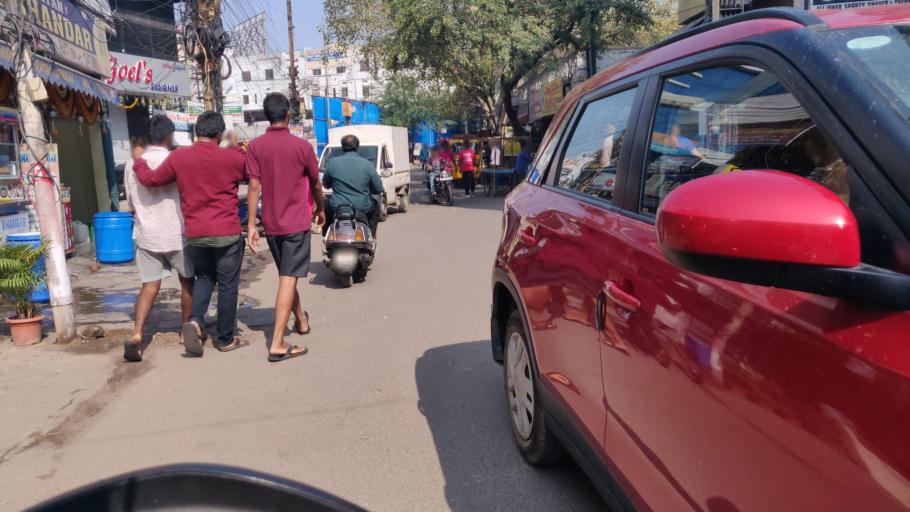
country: IN
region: Telangana
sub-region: Rangareddi
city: Gaddi Annaram
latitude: 17.3675
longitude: 78.5250
